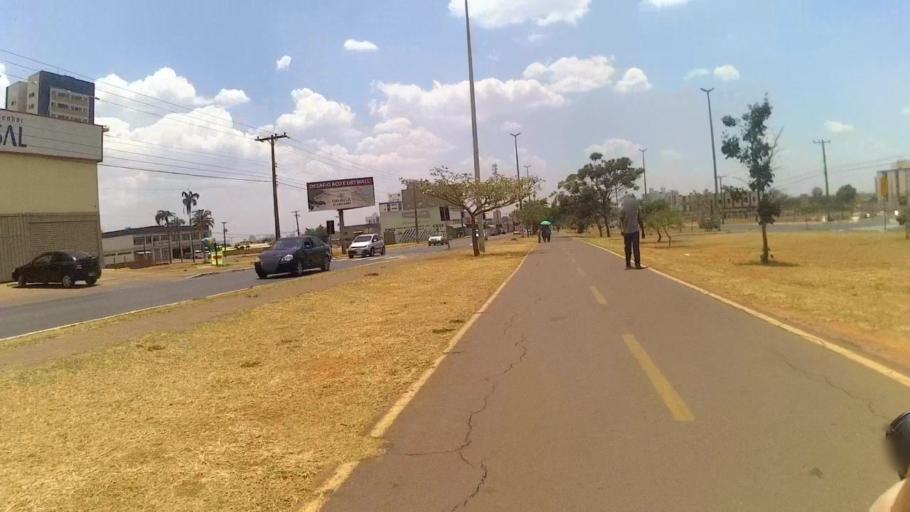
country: BR
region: Federal District
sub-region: Brasilia
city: Brasilia
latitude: -15.8751
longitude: -48.0777
